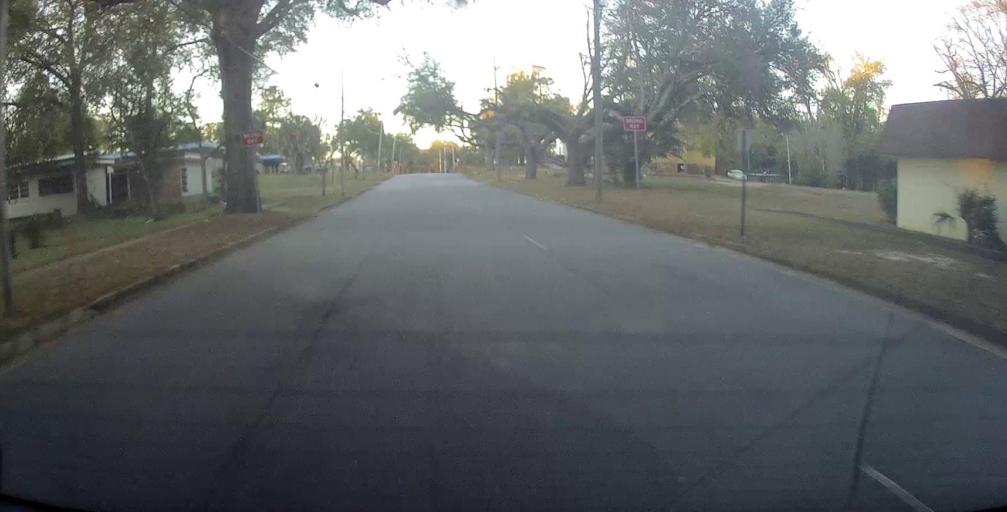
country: US
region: Georgia
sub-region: Dougherty County
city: Albany
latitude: 31.5710
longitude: -84.1619
